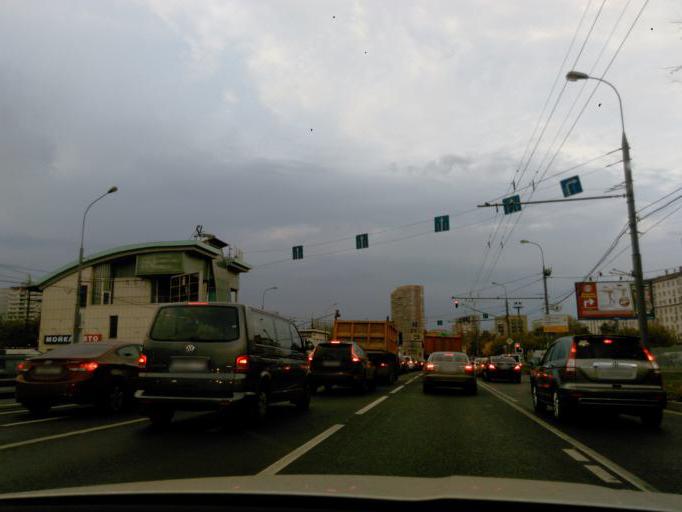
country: RU
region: Moscow
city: Likhobory
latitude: 55.8272
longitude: 37.5727
